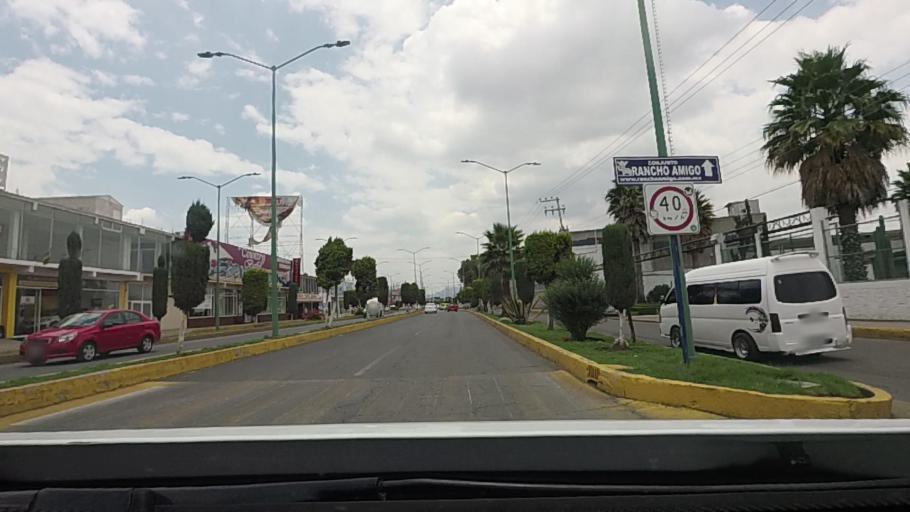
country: MX
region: Mexico
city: Chalco de Diaz Covarrubias
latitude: 19.2566
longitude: -98.8883
